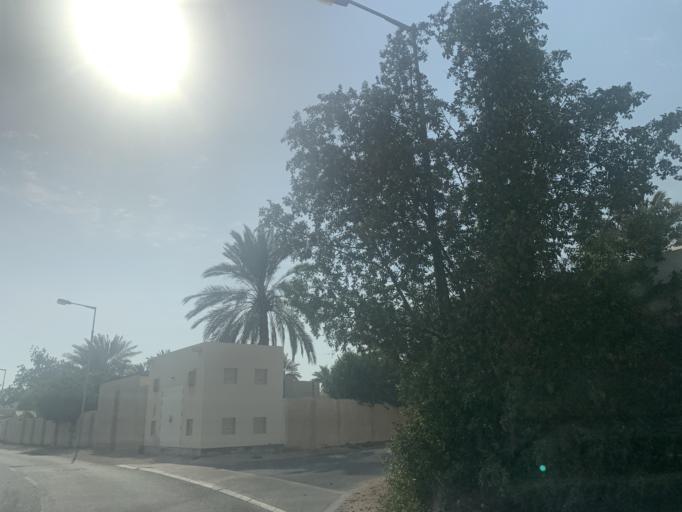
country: BH
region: Manama
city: Jidd Hafs
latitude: 26.2156
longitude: 50.4942
